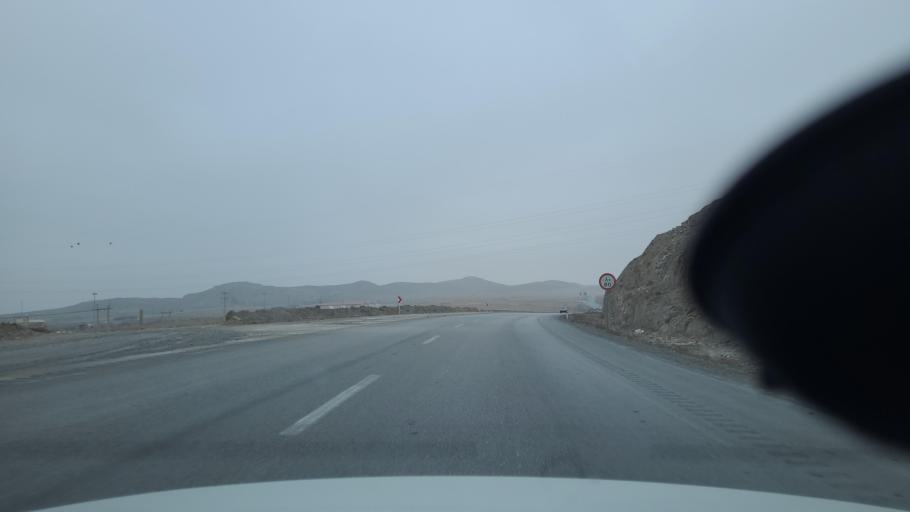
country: IR
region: Razavi Khorasan
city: Fariman
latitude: 35.9937
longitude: 59.7535
